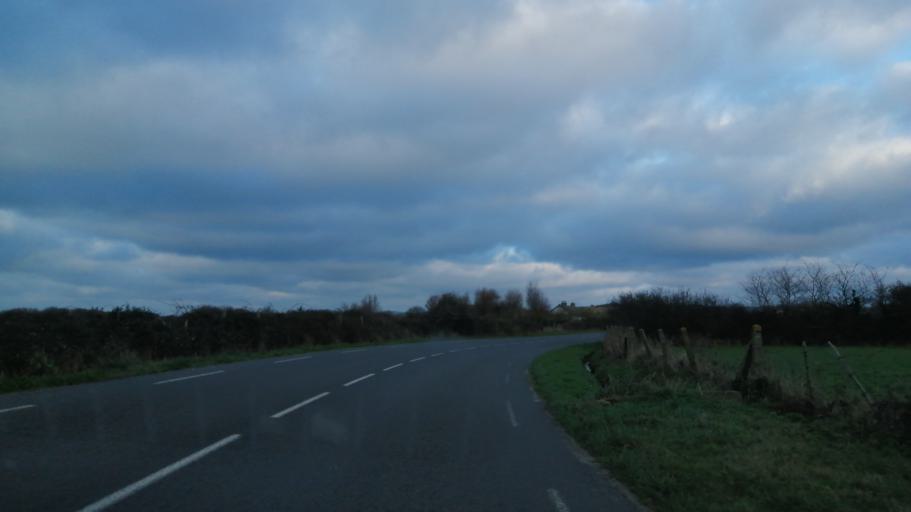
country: FR
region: Nord-Pas-de-Calais
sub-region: Departement du Pas-de-Calais
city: Wissant
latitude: 50.8701
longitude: 1.6342
